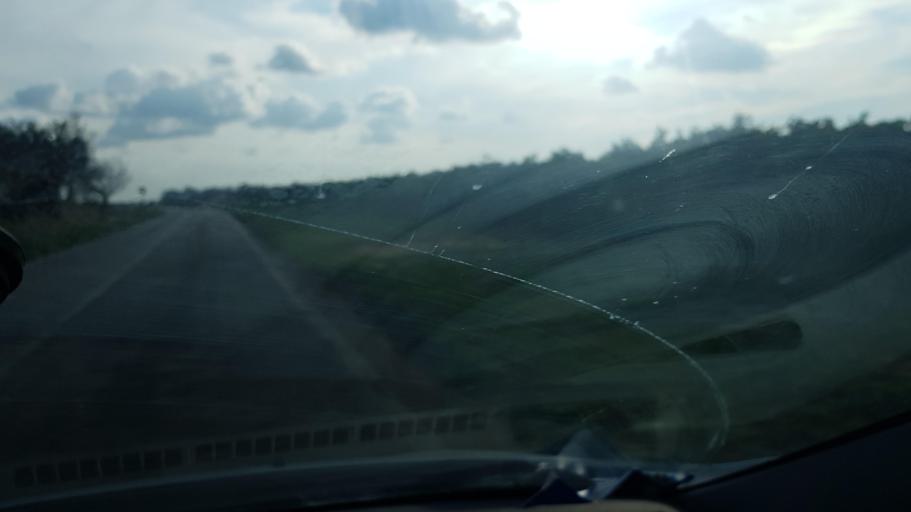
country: IT
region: Apulia
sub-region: Provincia di Brindisi
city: San Donaci
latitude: 40.4362
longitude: 17.9529
